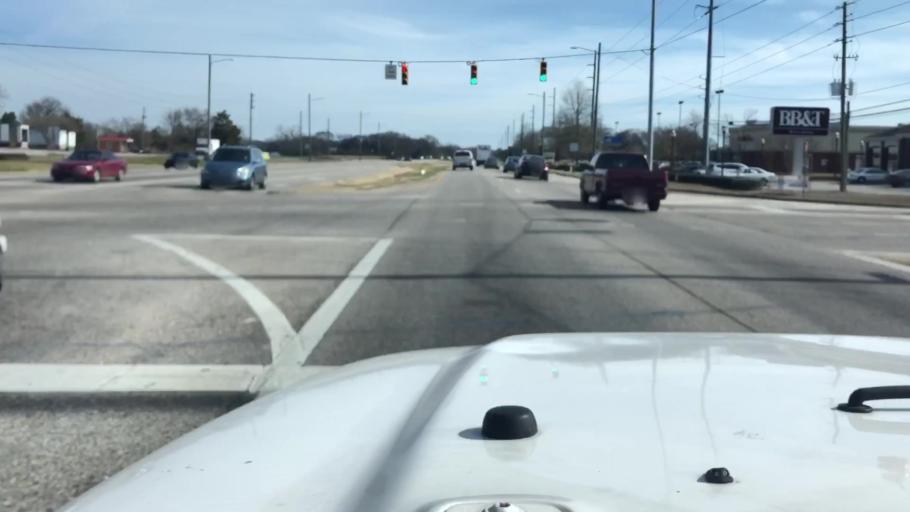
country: US
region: Alabama
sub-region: Elmore County
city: Blue Ridge
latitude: 32.3825
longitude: -86.1736
